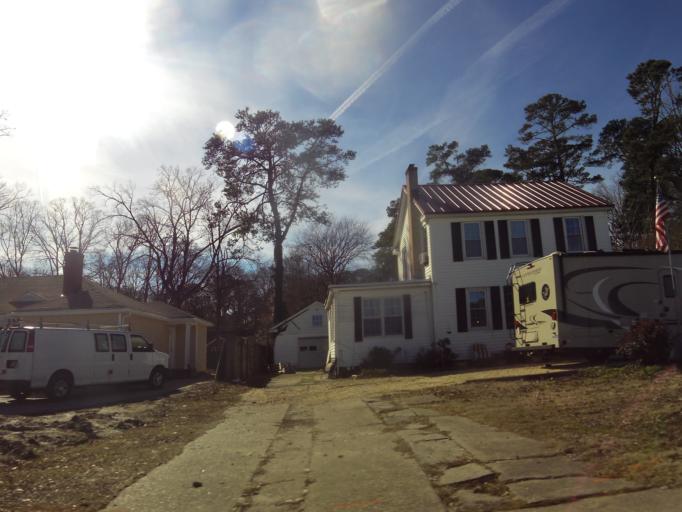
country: US
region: Virginia
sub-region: City of Newport News
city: Newport News
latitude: 37.0408
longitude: -76.4705
